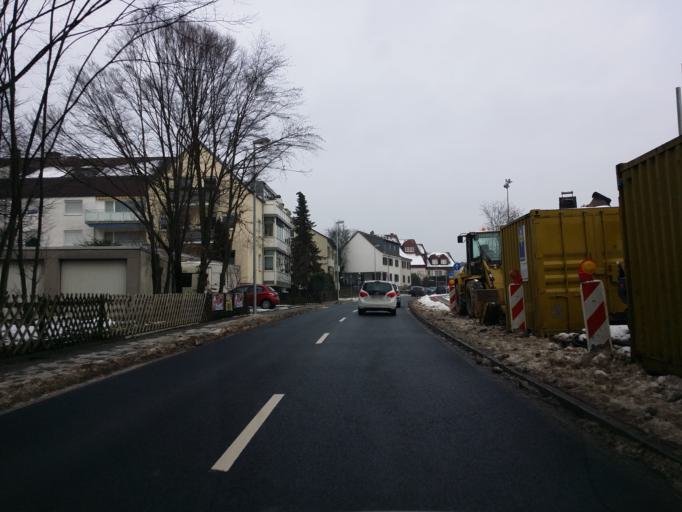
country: DE
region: Hesse
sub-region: Regierungsbezirk Darmstadt
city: Hofheim am Taunus
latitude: 50.0848
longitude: 8.4535
